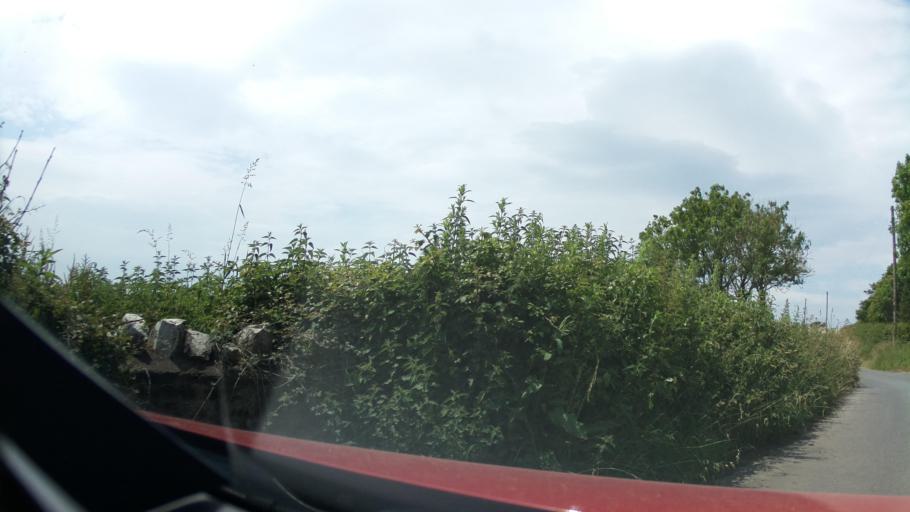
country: GB
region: Wales
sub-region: Vale of Glamorgan
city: Wick
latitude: 51.4260
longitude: -3.5564
